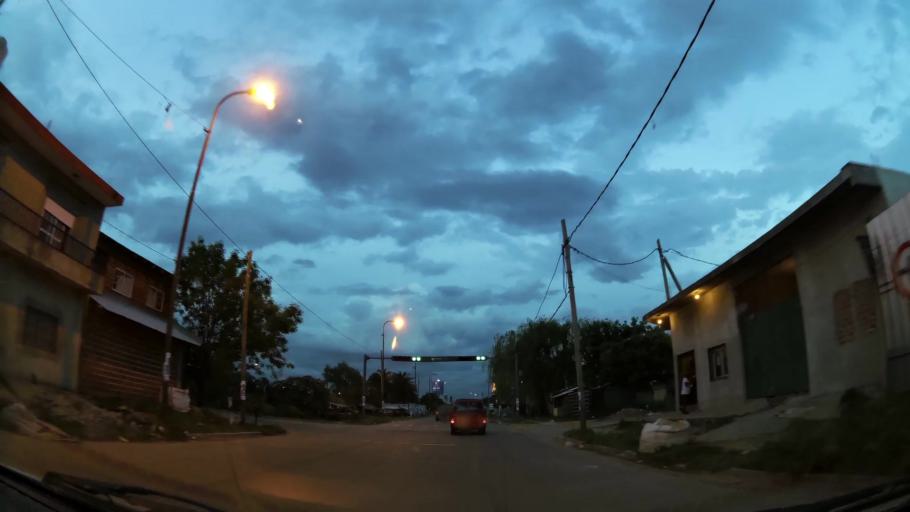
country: AR
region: Buenos Aires
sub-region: Partido de Quilmes
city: Quilmes
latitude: -34.7198
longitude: -58.2354
